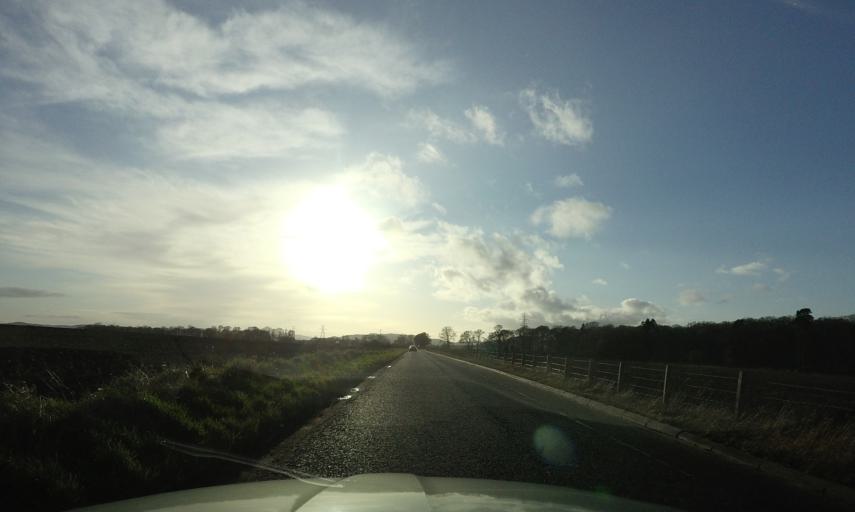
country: GB
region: Scotland
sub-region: Fife
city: Newburgh
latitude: 56.3789
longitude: -3.2661
